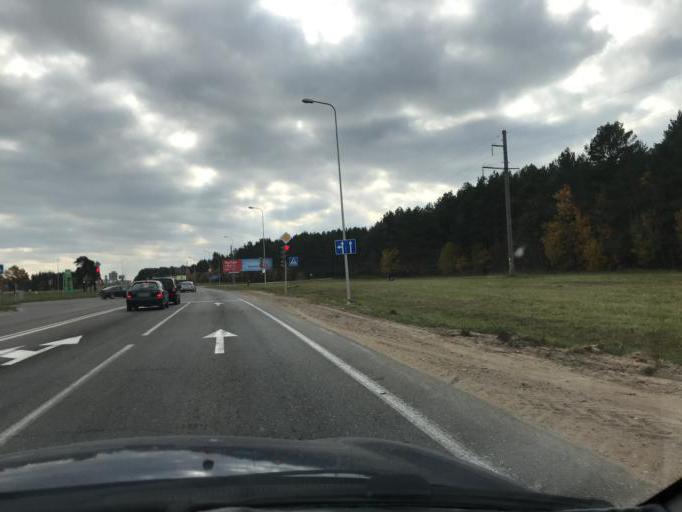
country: BY
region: Grodnenskaya
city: Lida
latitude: 53.8935
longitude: 25.2517
